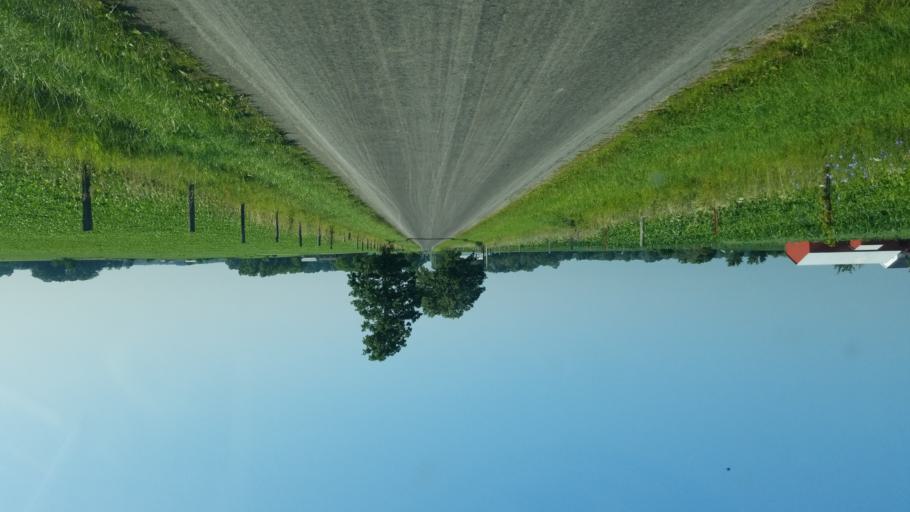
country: US
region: Ohio
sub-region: Hardin County
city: Kenton
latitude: 40.5698
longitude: -83.5275
